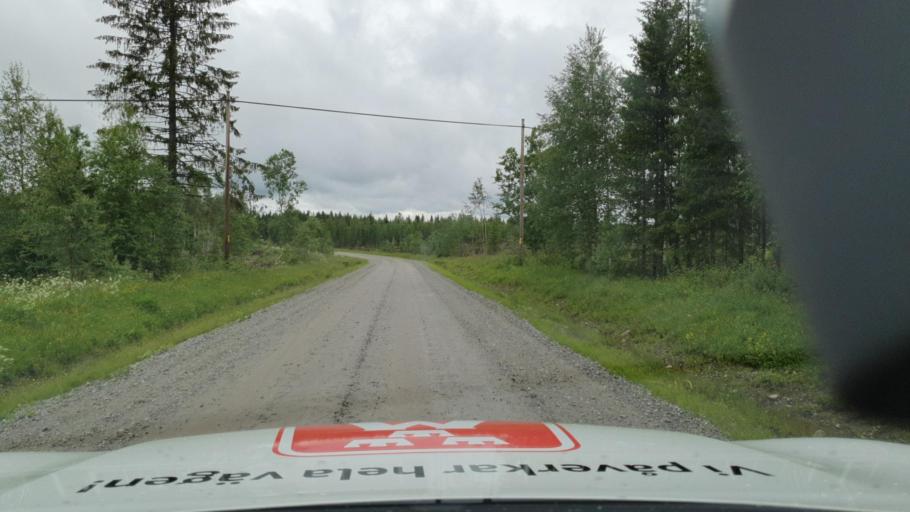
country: SE
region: Vaesterbotten
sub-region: Dorotea Kommun
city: Dorotea
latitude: 64.0873
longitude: 16.6771
